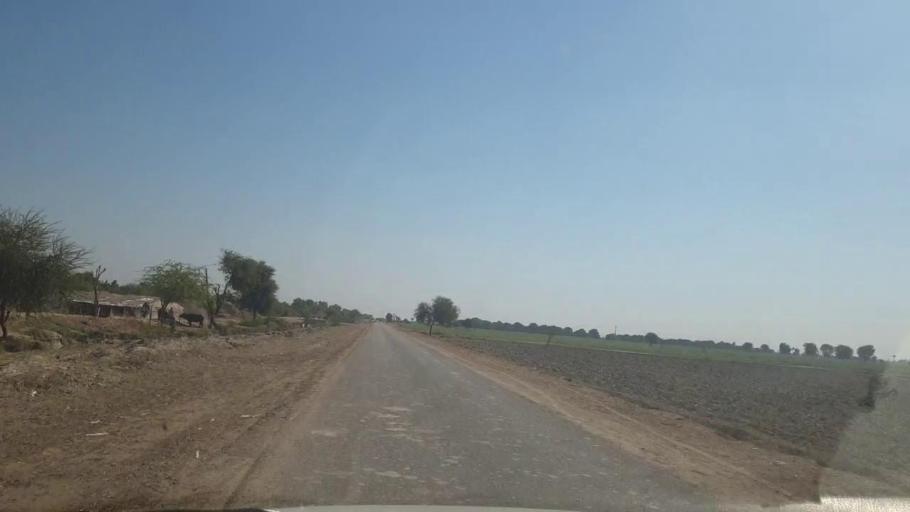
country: PK
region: Sindh
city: Mirpur Khas
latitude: 25.4681
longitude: 69.1777
